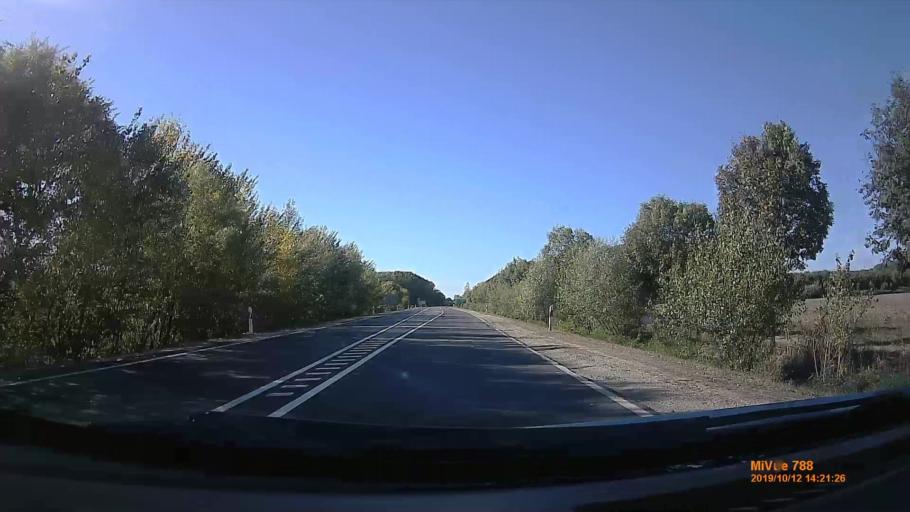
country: HU
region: Hajdu-Bihar
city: Biharkeresztes
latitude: 47.1390
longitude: 21.7339
